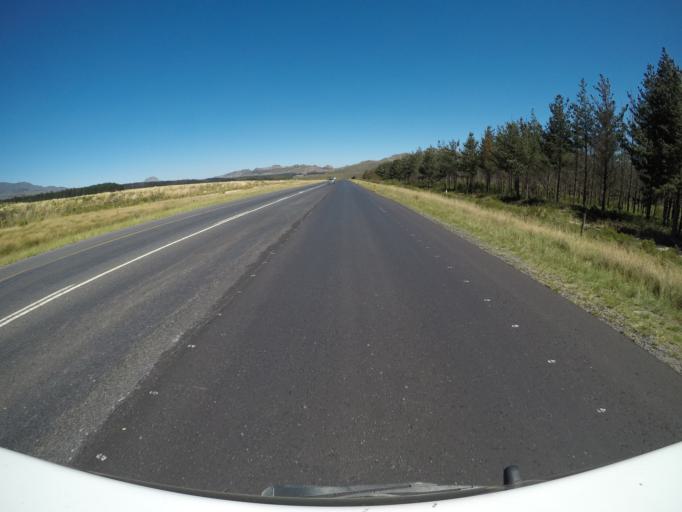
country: ZA
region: Western Cape
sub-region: Overberg District Municipality
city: Grabouw
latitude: -34.1523
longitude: 18.9628
